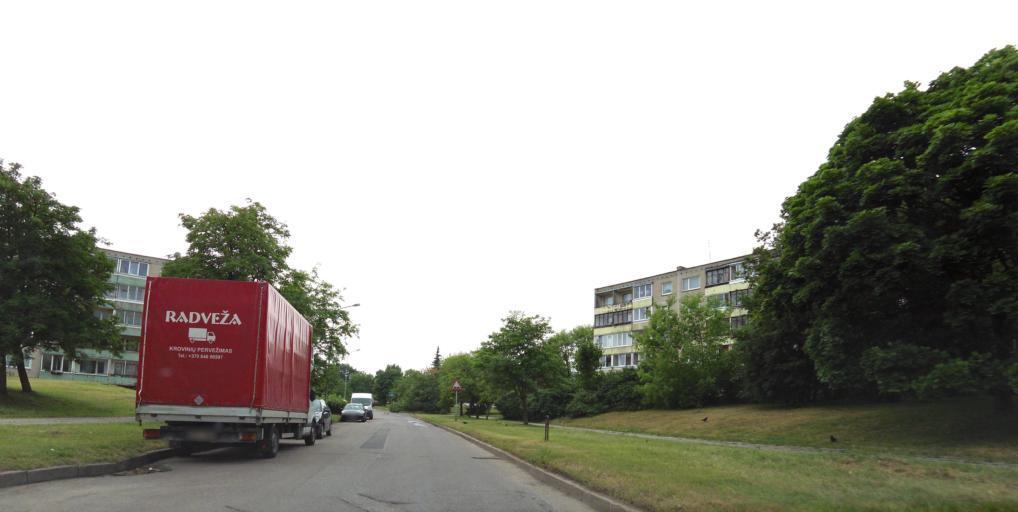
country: LT
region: Vilnius County
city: Justiniskes
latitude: 54.6931
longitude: 25.2119
